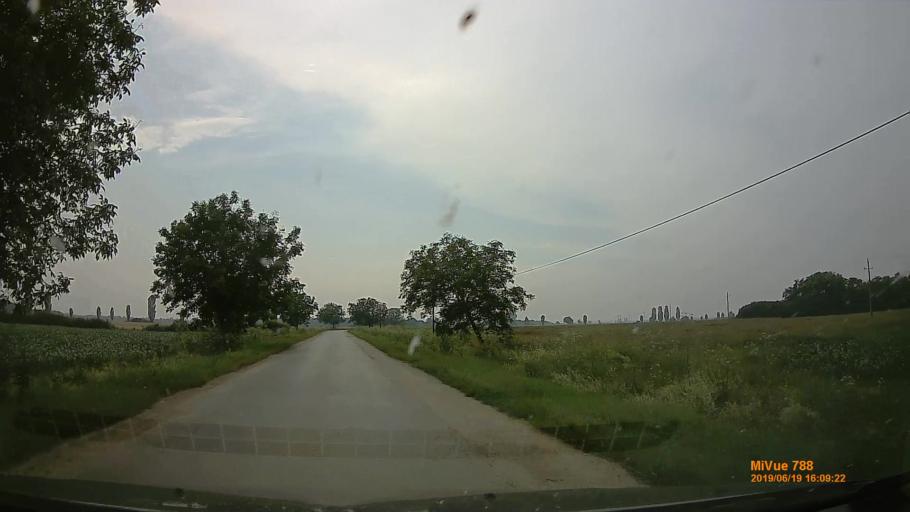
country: HU
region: Baranya
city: Szigetvar
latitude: 46.0726
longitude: 17.7709
